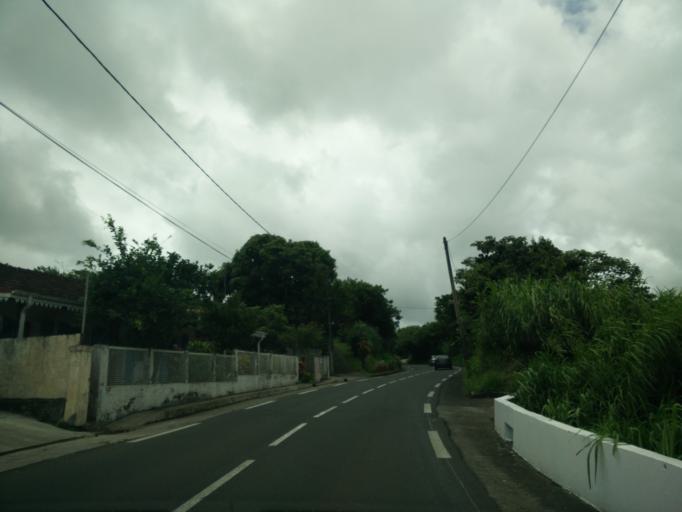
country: MQ
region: Martinique
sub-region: Martinique
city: Le Morne-Rouge
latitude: 14.7636
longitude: -61.1519
